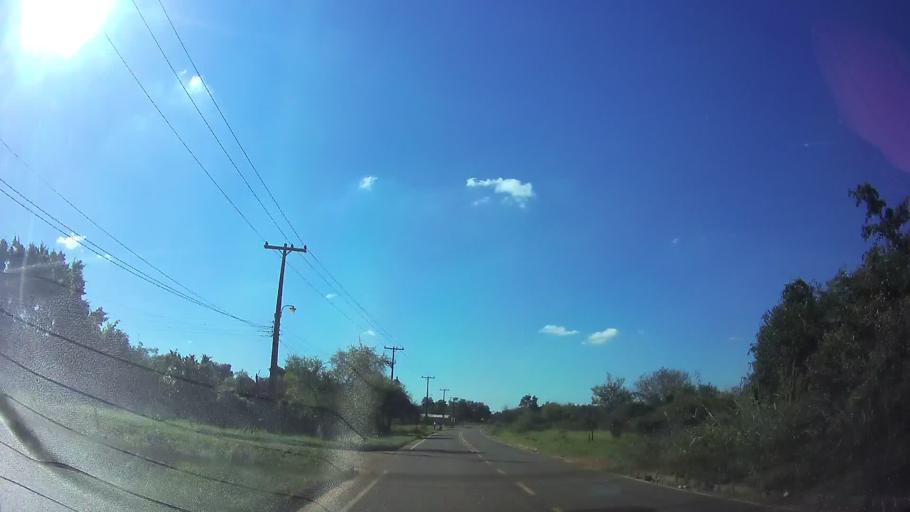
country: PY
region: Central
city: Limpio
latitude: -25.1933
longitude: -57.4763
